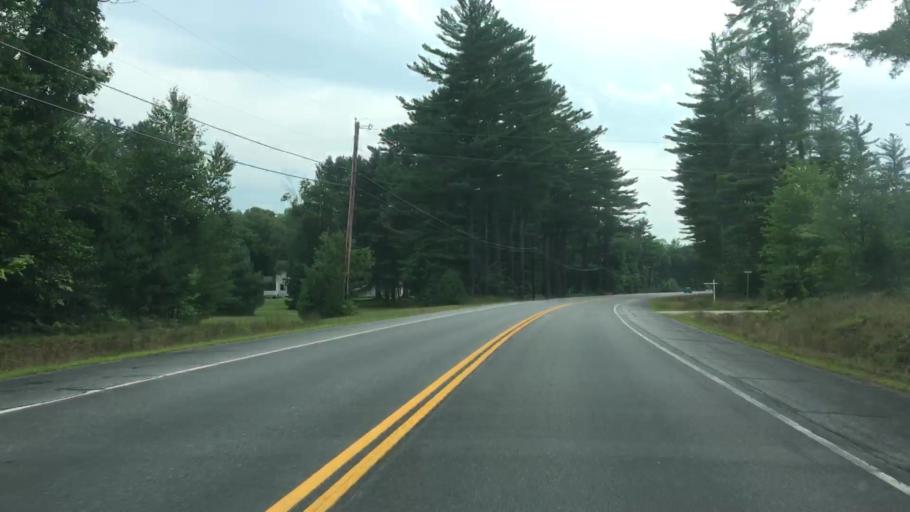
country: US
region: Maine
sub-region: Oxford County
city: Bethel
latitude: 44.4904
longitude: -70.6975
